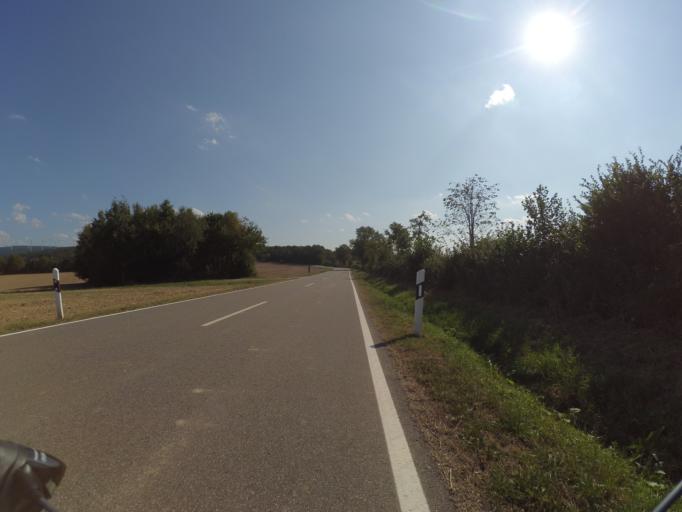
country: DE
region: Rheinland-Pfalz
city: Wintrich
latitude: 49.8714
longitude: 6.9626
